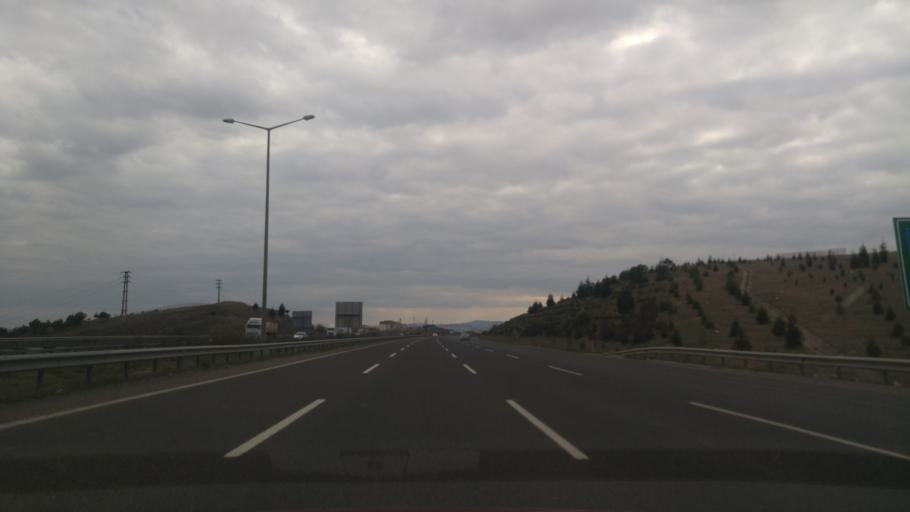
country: TR
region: Ankara
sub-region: Goelbasi
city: Golbasi
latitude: 39.8024
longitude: 32.7926
